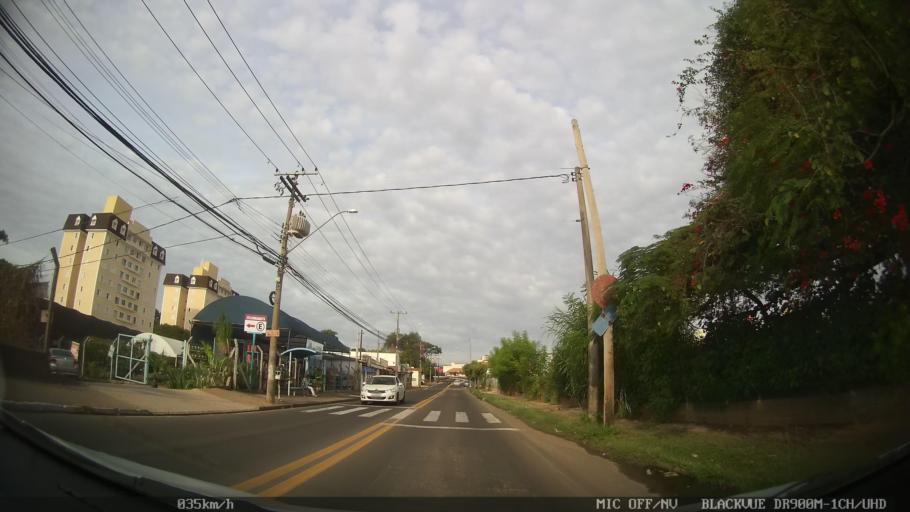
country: BR
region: Sao Paulo
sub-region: Piracicaba
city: Piracicaba
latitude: -22.7420
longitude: -47.6172
